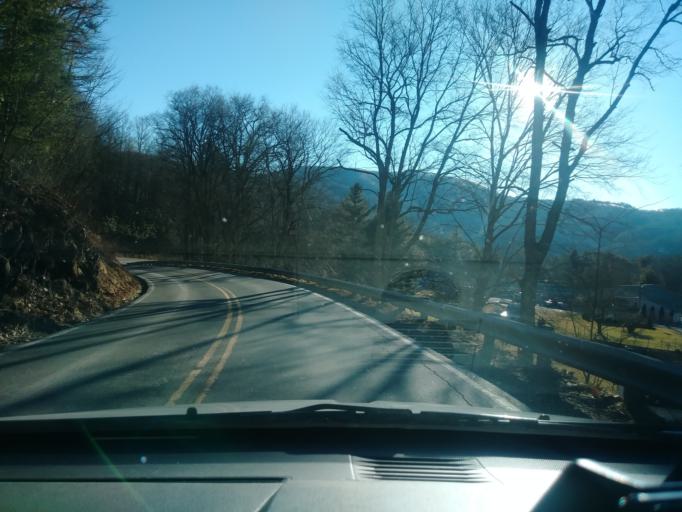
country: US
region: North Carolina
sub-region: Avery County
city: Banner Elk
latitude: 36.1610
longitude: -81.8842
